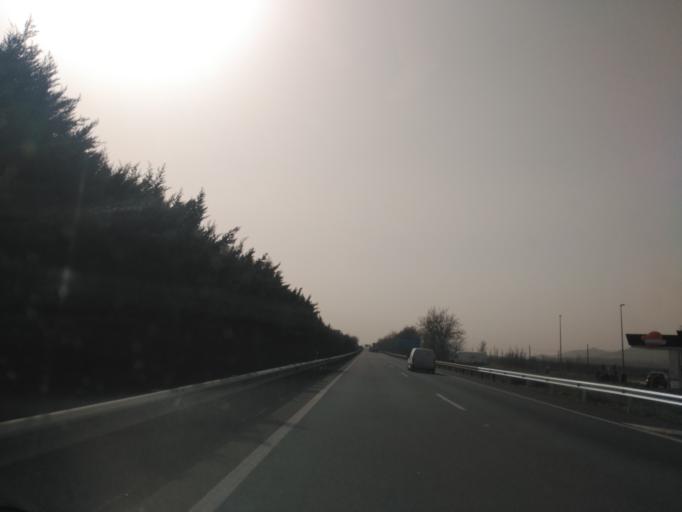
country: ES
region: Castille and Leon
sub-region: Provincia de Palencia
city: Venta de Banos
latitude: 41.9139
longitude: -4.5110
